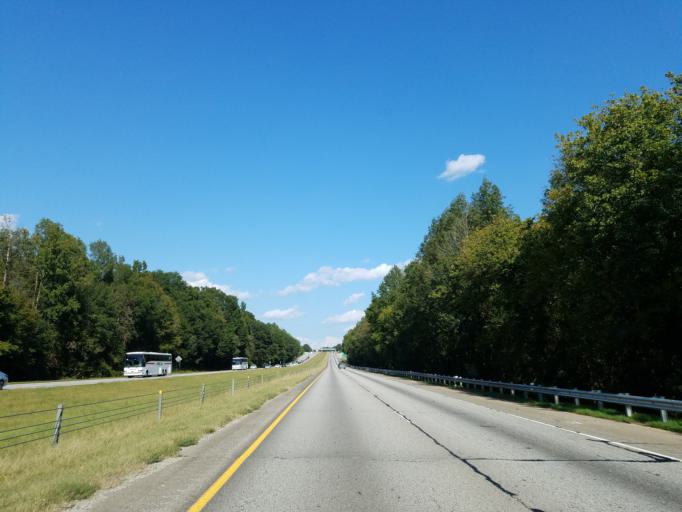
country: US
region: Georgia
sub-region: Franklin County
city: Carnesville
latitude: 34.3708
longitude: -83.2709
